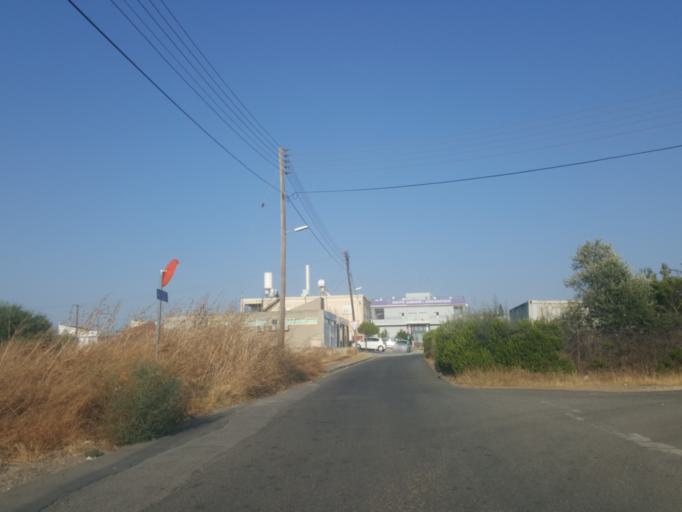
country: CY
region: Lefkosia
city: Tseri
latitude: 35.1160
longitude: 33.3314
